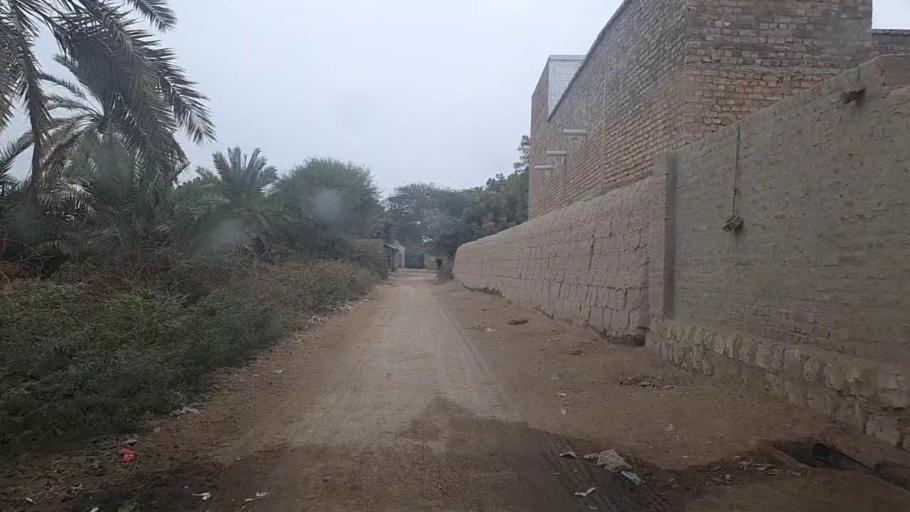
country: PK
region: Sindh
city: Gambat
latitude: 27.3625
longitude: 68.5977
